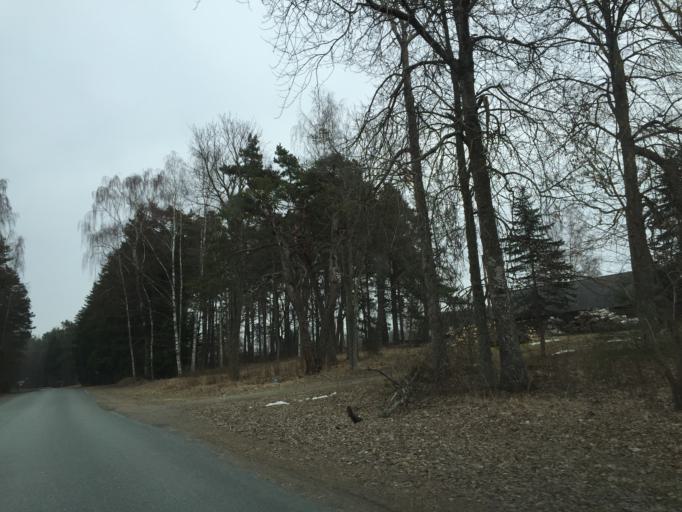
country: LV
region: Salacgrivas
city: Ainazi
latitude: 58.0176
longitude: 24.4517
